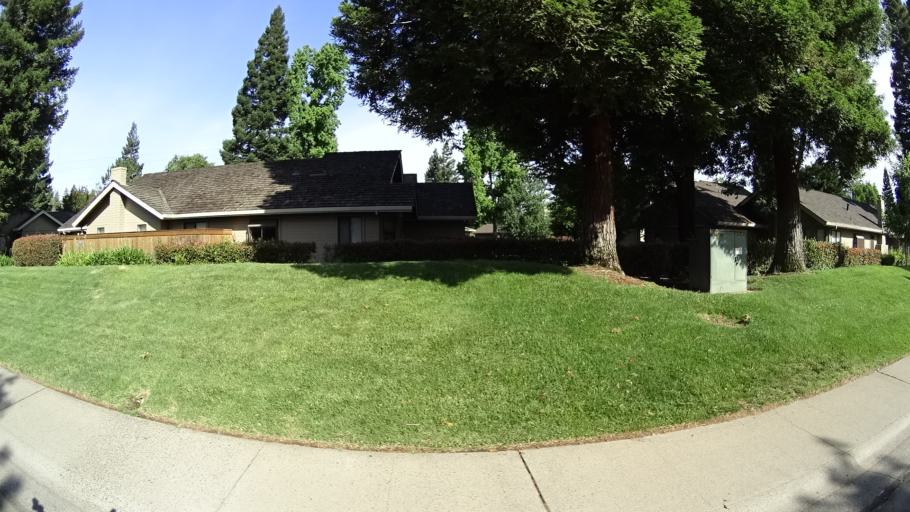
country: US
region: California
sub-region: Sacramento County
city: Rosemont
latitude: 38.5633
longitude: -121.4066
